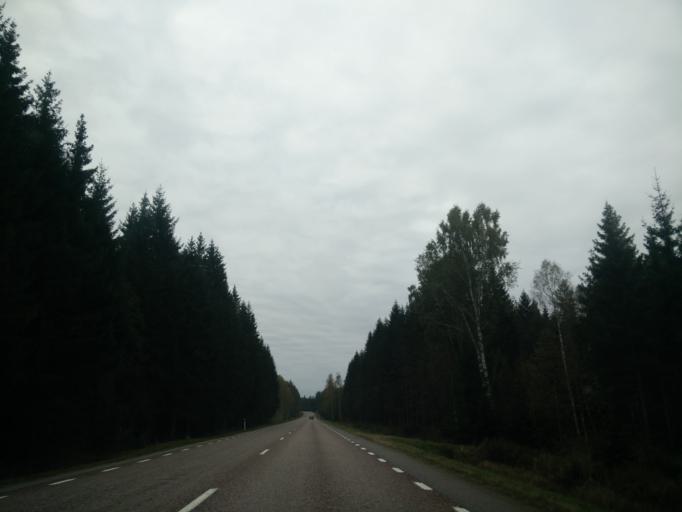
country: SE
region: Gaevleborg
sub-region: Gavle Kommun
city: Norrsundet
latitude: 60.8434
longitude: 17.1991
